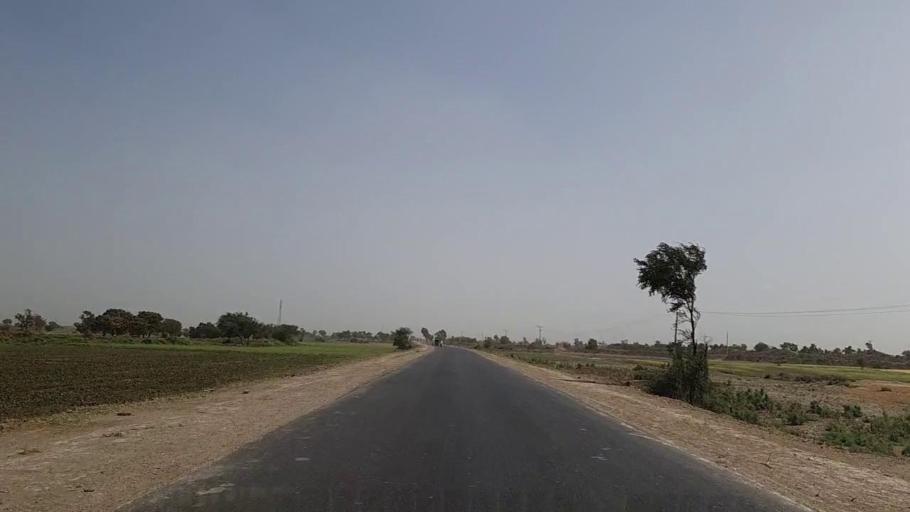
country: PK
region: Sindh
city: Tando Bago
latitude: 24.8318
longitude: 68.8926
